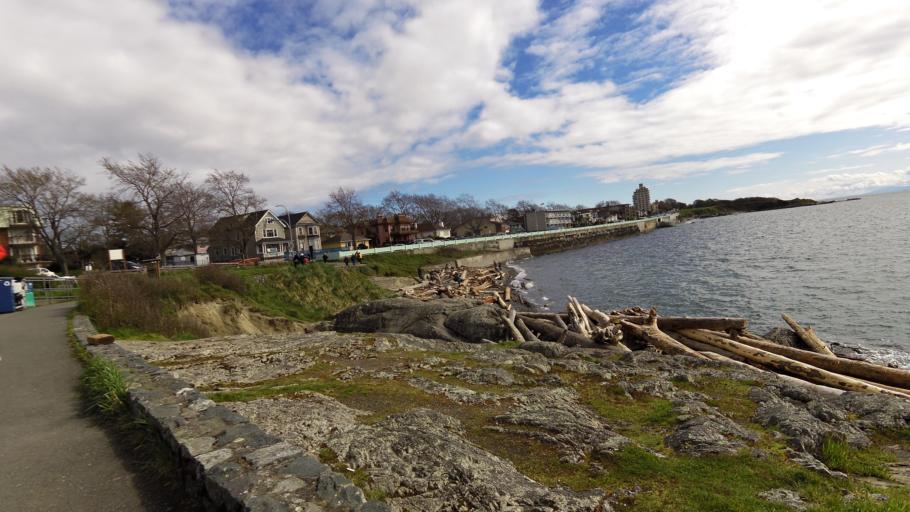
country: CA
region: British Columbia
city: Victoria
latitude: 48.4151
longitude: -123.3850
